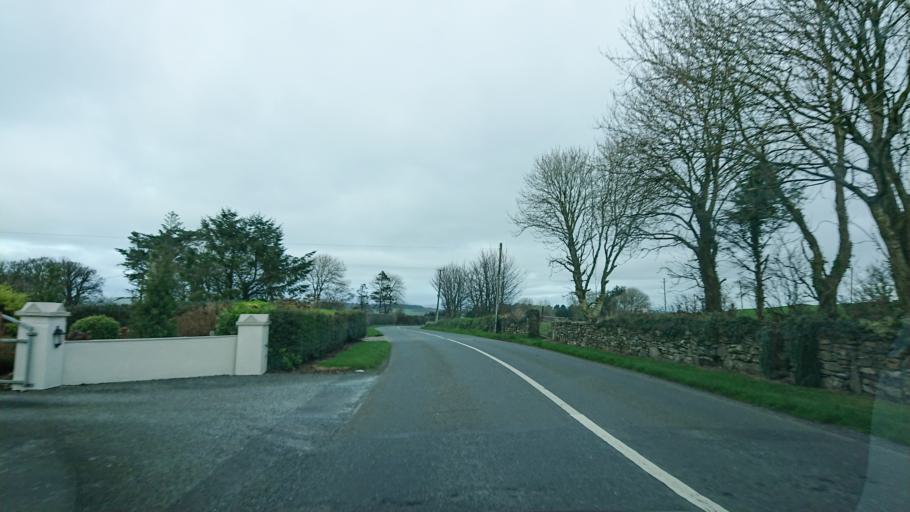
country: IE
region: Leinster
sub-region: Kilkenny
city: Mooncoin
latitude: 52.2005
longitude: -7.2669
